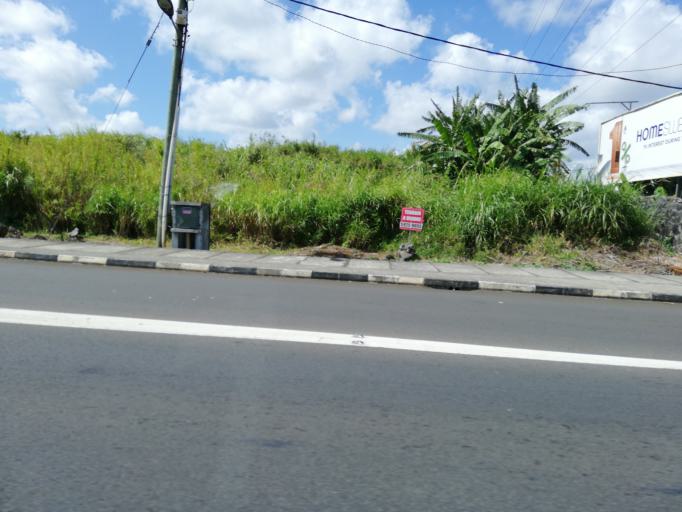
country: MU
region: Plaines Wilhems
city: Ebene
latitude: -20.2501
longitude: 57.4930
